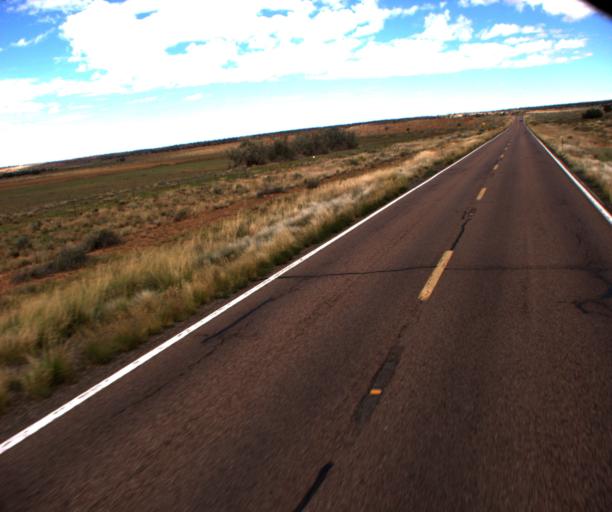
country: US
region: Arizona
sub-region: Navajo County
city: Heber-Overgaard
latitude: 34.6199
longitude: -110.3709
